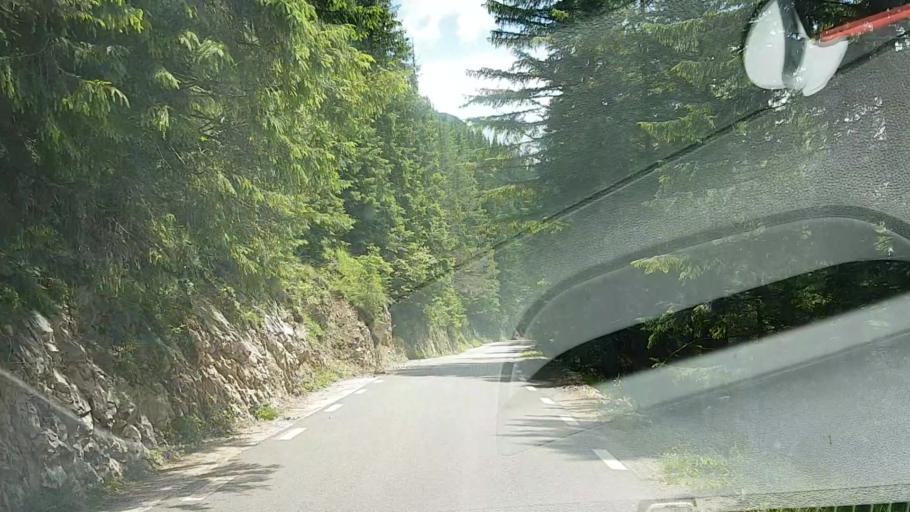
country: RO
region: Suceava
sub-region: Municipiul Campulung Moldovenesc
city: Campulung Moldovenesc
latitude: 47.4493
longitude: 25.5518
